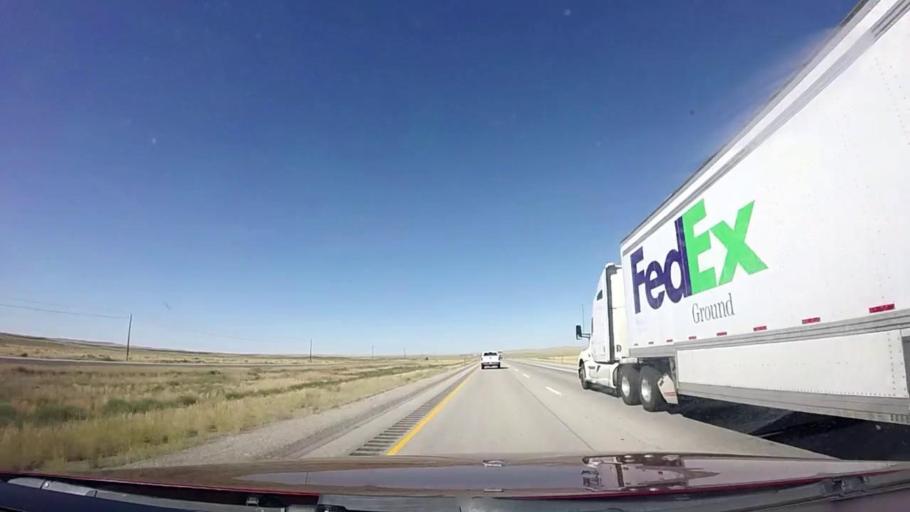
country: US
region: Wyoming
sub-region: Carbon County
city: Rawlins
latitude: 41.7807
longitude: -107.4328
